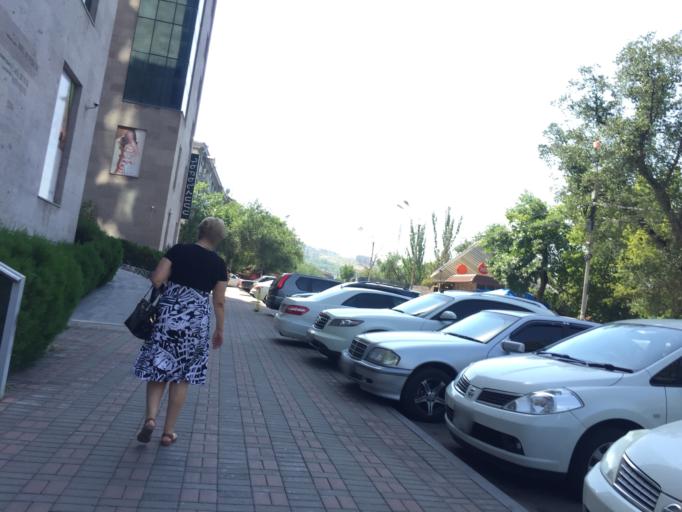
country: AM
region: Yerevan
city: Yerevan
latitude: 40.1879
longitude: 44.5209
